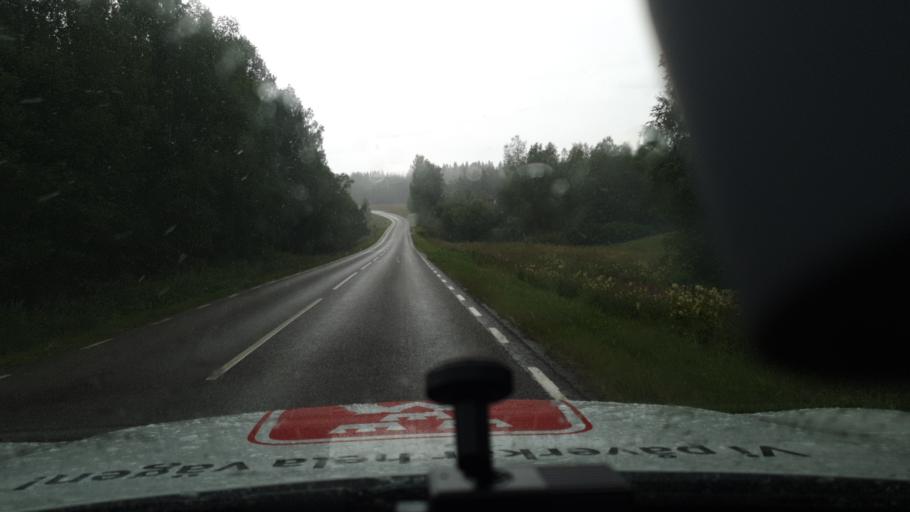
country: SE
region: Vaermland
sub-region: Sunne Kommun
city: Sunne
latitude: 59.7899
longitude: 13.0828
